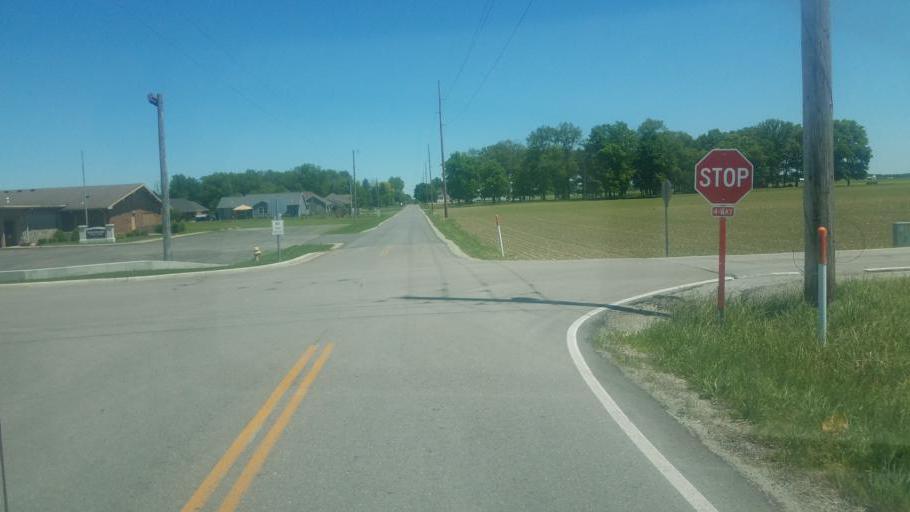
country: US
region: Ohio
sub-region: Darke County
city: Versailles
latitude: 40.2264
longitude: -84.4144
